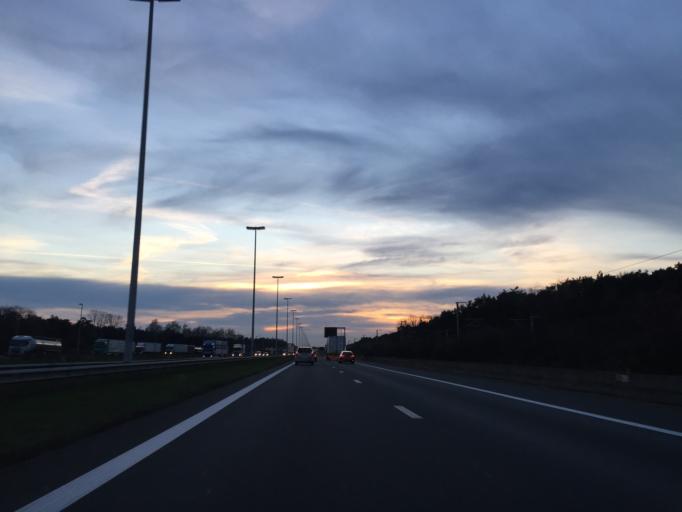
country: BE
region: Flanders
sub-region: Provincie Antwerpen
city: Brecht
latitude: 51.3234
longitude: 4.5870
